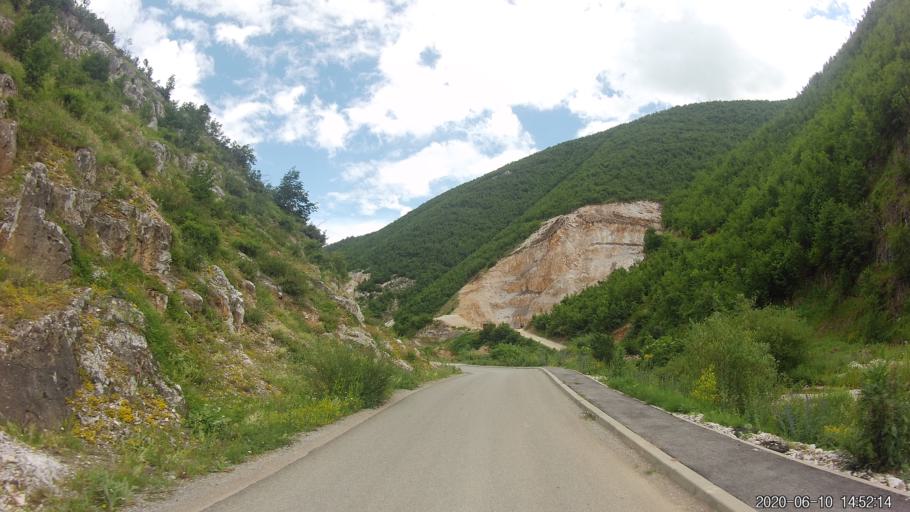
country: XK
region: Ferizaj
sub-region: Komuna e Shtimes
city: Shtime
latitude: 42.4006
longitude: 20.9814
